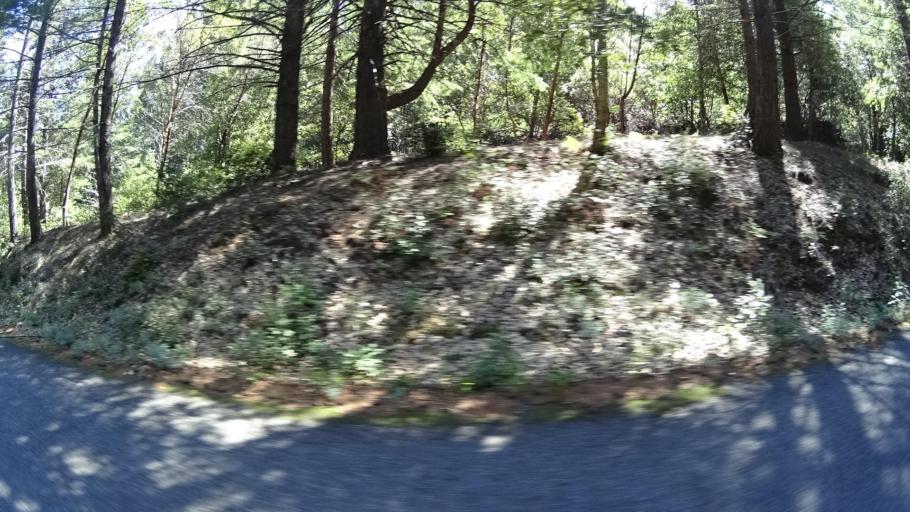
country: US
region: California
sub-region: Humboldt County
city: Redway
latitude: 40.1763
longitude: -124.0893
